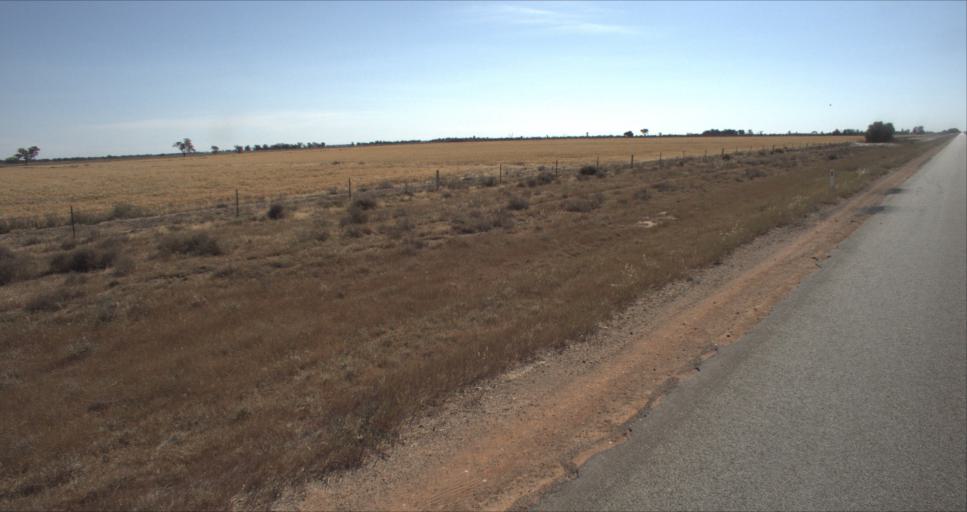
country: AU
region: New South Wales
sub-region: Leeton
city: Leeton
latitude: -34.4960
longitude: 146.3892
